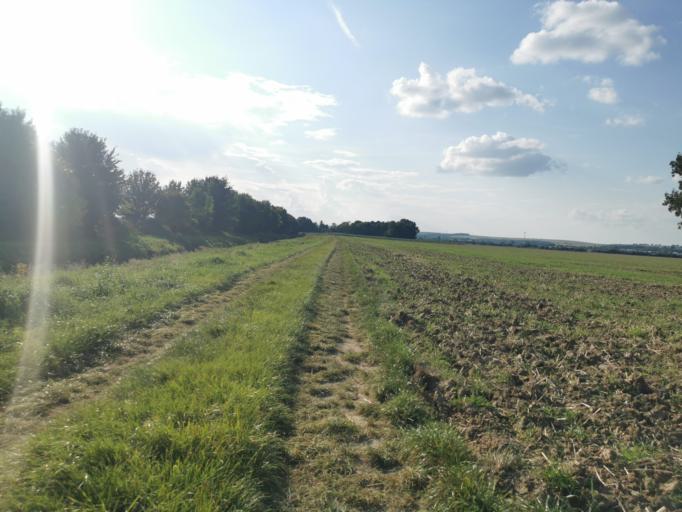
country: SK
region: Trnavsky
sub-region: Okres Senica
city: Senica
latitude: 48.6682
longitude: 17.2857
